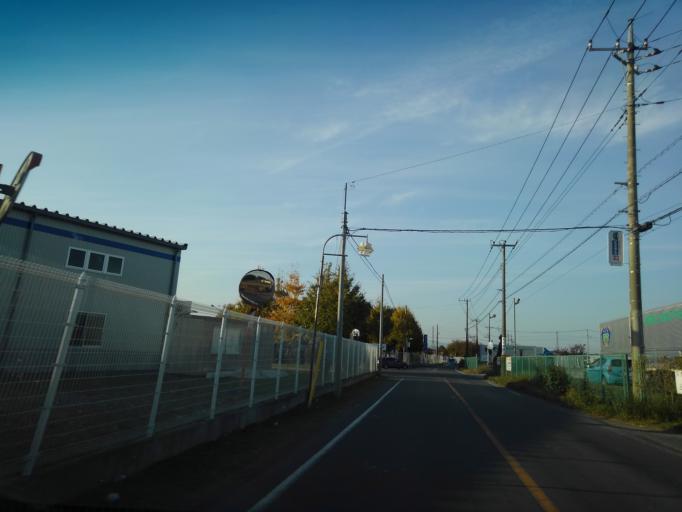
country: JP
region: Saitama
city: Hanno
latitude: 35.7986
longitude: 139.3405
